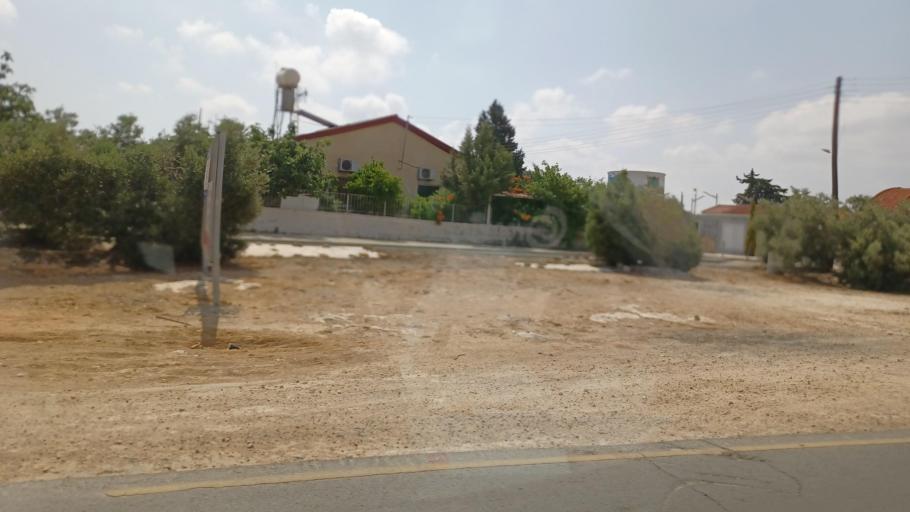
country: CY
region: Ammochostos
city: Deryneia
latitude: 35.0505
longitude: 33.9574
